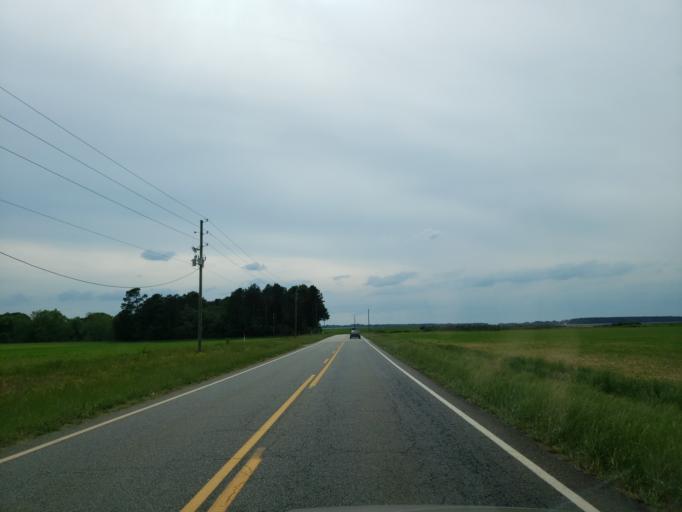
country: US
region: Georgia
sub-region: Macon County
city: Marshallville
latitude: 32.3665
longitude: -83.9122
